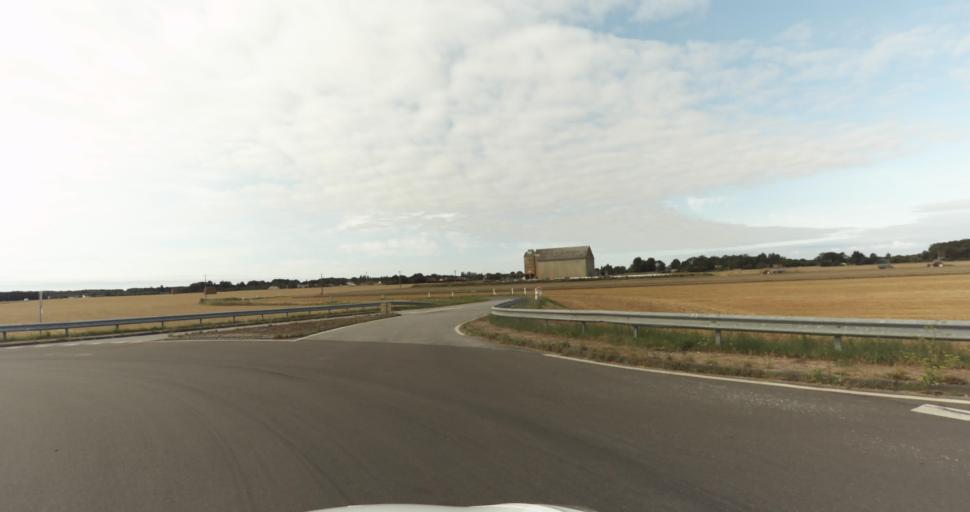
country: FR
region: Haute-Normandie
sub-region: Departement de l'Eure
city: La Madeleine-de-Nonancourt
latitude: 48.8348
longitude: 1.1816
